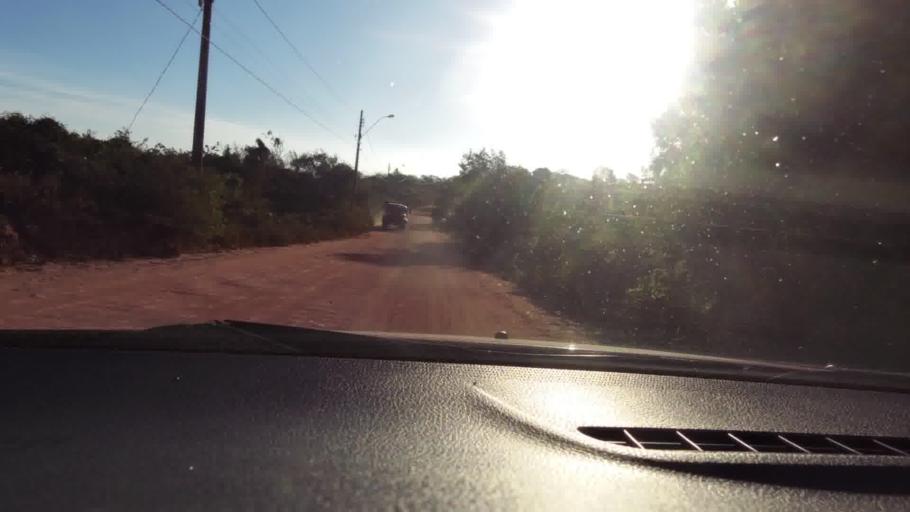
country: BR
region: Espirito Santo
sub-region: Guarapari
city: Guarapari
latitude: -20.5522
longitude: -40.4167
